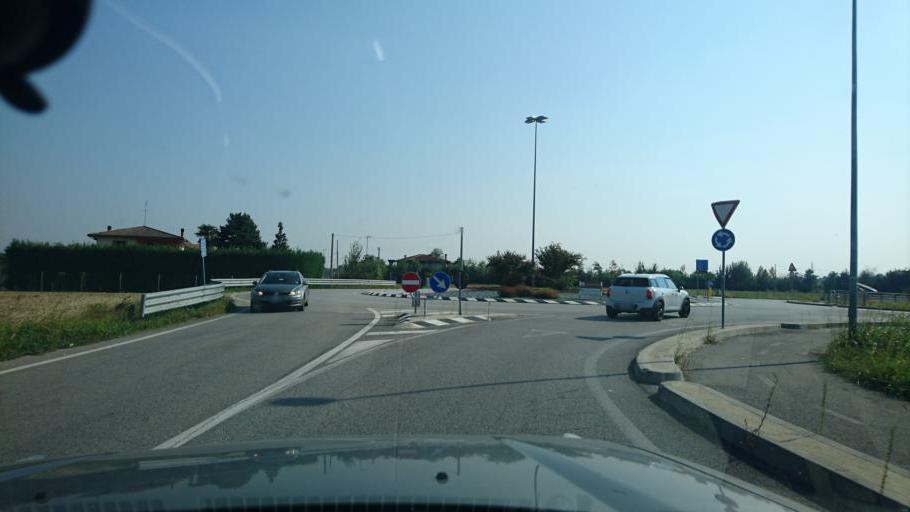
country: IT
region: Veneto
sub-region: Provincia di Padova
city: Ronchi di Campanile
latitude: 45.4583
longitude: 11.7785
